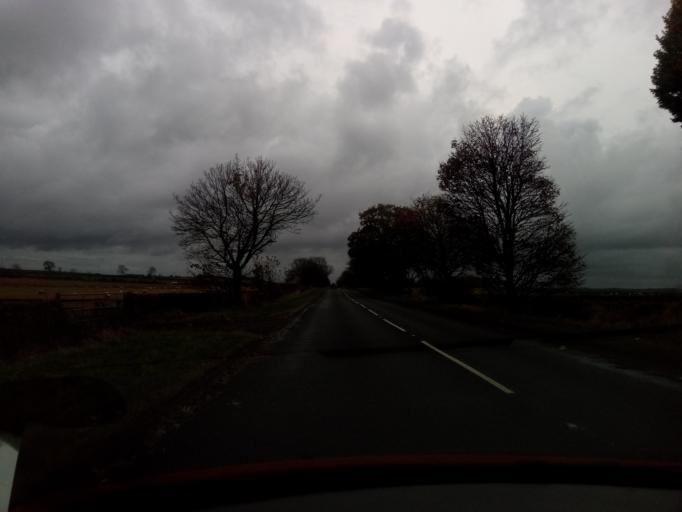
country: GB
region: England
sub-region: County Durham
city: Hamsterley
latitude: 54.6939
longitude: -1.7853
